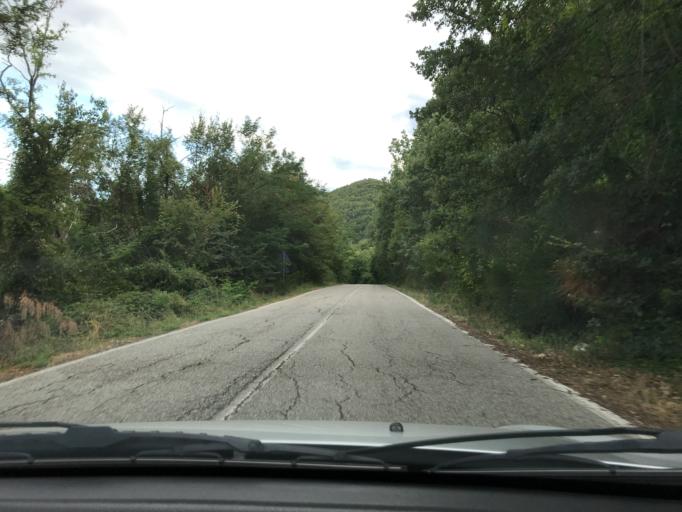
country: IT
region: Umbria
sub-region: Provincia di Terni
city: Montecchio
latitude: 42.6644
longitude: 12.3361
